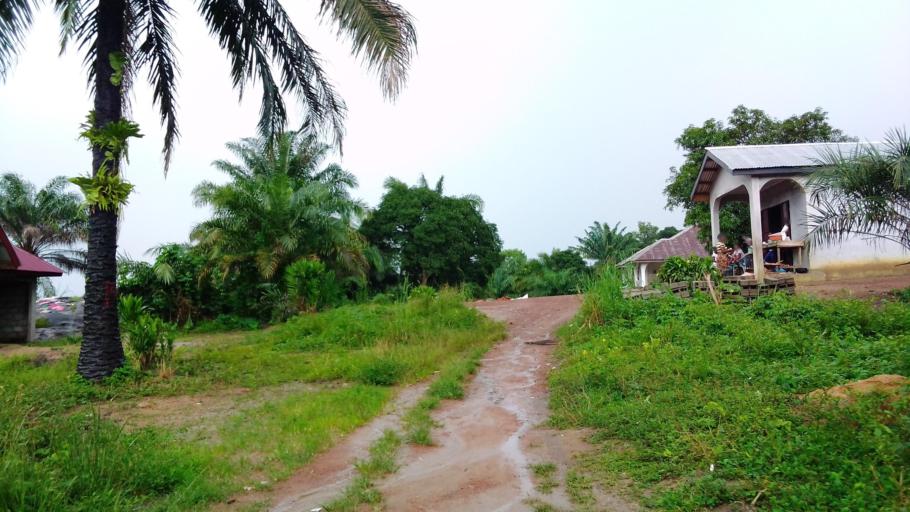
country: SL
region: Eastern Province
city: Kenema
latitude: 7.8796
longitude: -11.1720
